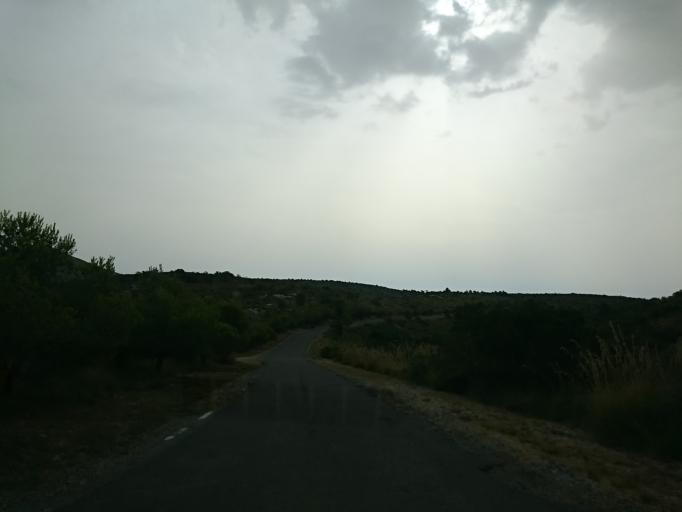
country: ES
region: Catalonia
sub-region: Provincia de Barcelona
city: Begues
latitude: 41.2815
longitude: 1.8954
